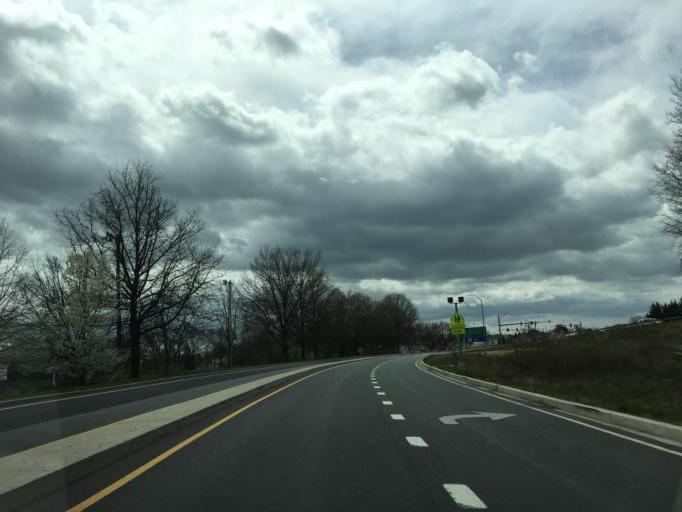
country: US
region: Maryland
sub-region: Frederick County
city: Frederick
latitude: 39.4356
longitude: -77.4089
